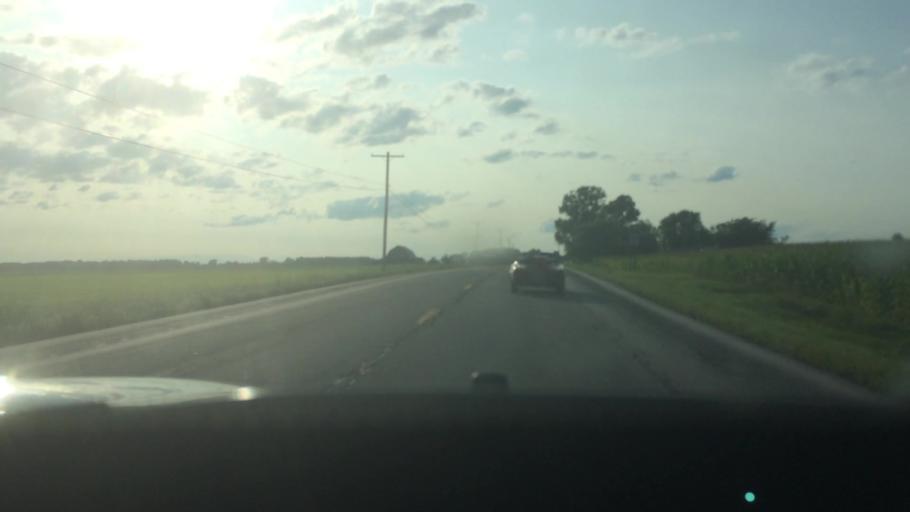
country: US
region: New York
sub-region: St. Lawrence County
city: Ogdensburg
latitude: 44.6616
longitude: -75.3382
